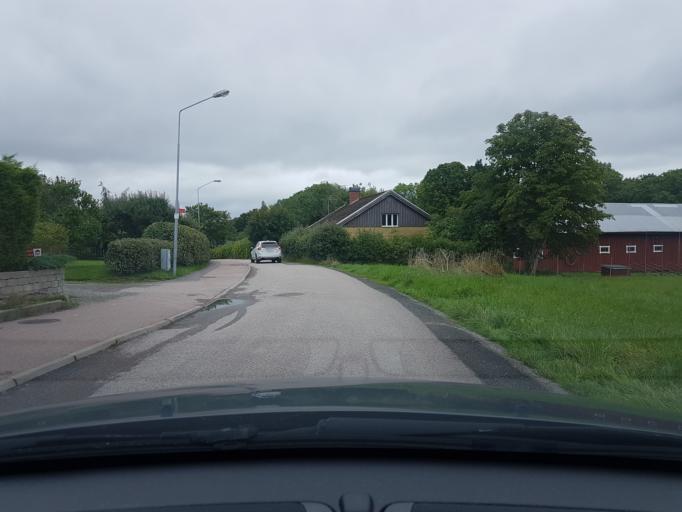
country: SE
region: Vaestra Goetaland
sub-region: Ale Kommun
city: Nodinge-Nol
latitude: 57.8917
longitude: 12.0573
